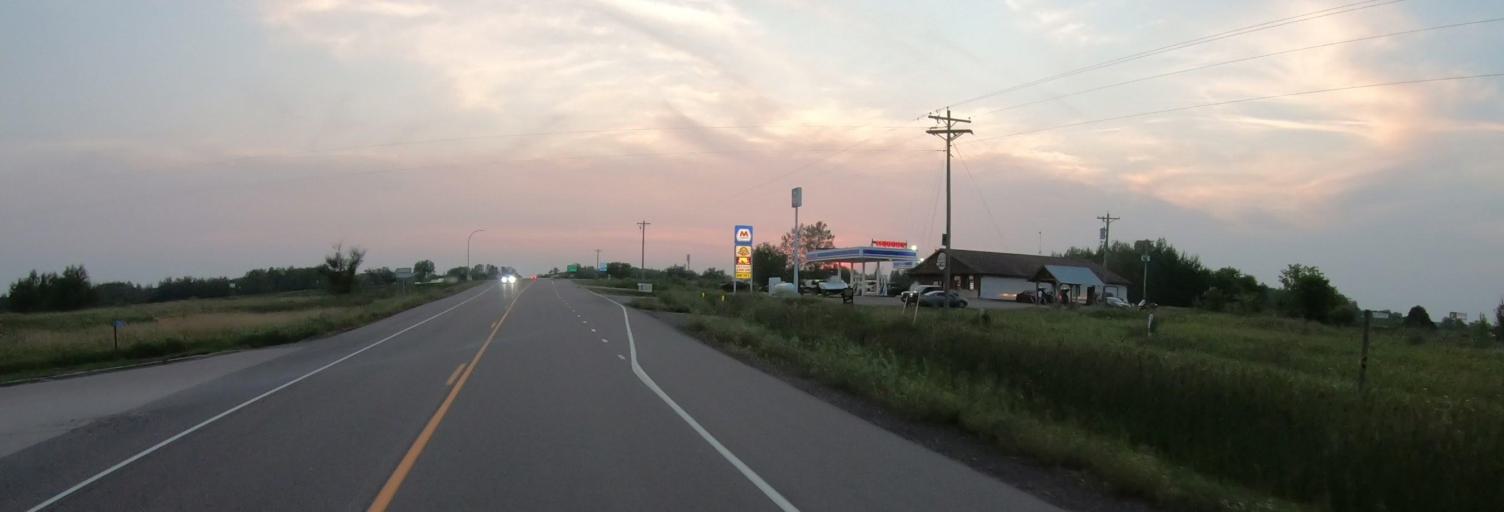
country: US
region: Minnesota
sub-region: Pine County
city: Rock Creek
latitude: 45.7667
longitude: -92.9862
